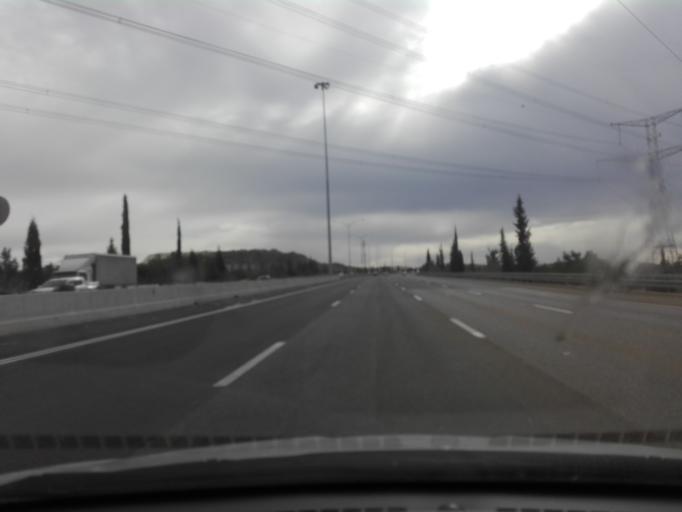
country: PS
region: West Bank
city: Rantis
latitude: 32.0247
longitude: 34.9631
